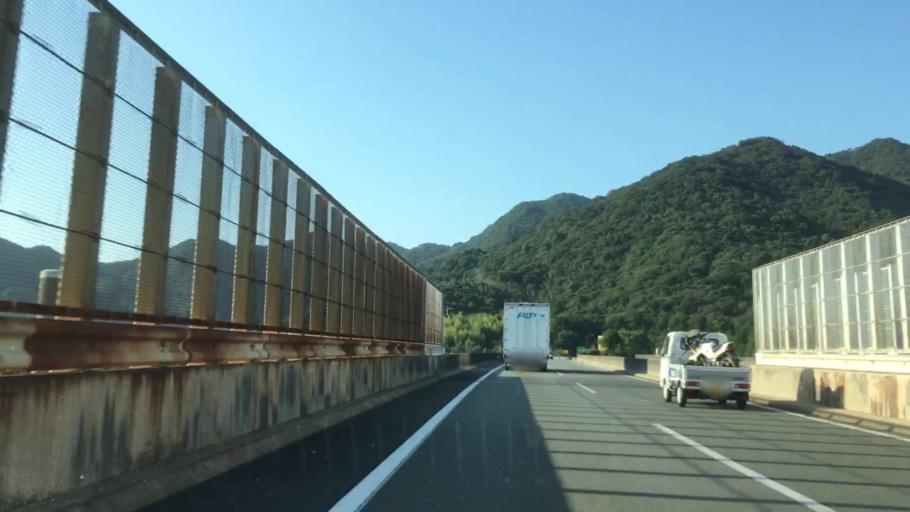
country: JP
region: Yamaguchi
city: Ogori-shimogo
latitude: 34.0973
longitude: 131.4526
